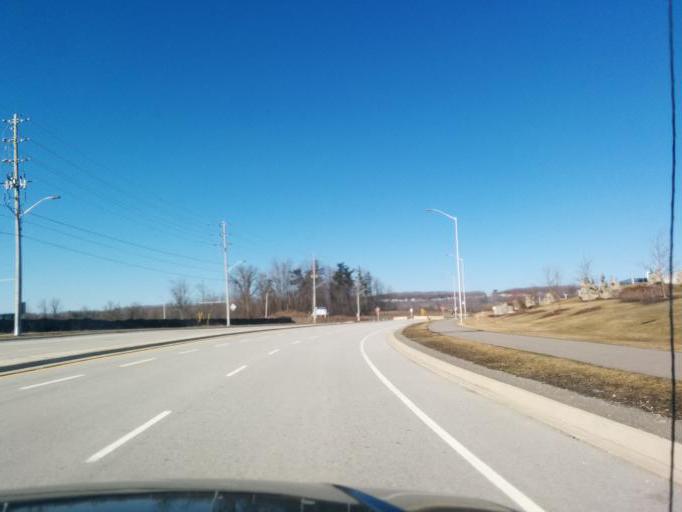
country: CA
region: Ontario
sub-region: Halton
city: Milton
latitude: 43.5299
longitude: -79.9197
